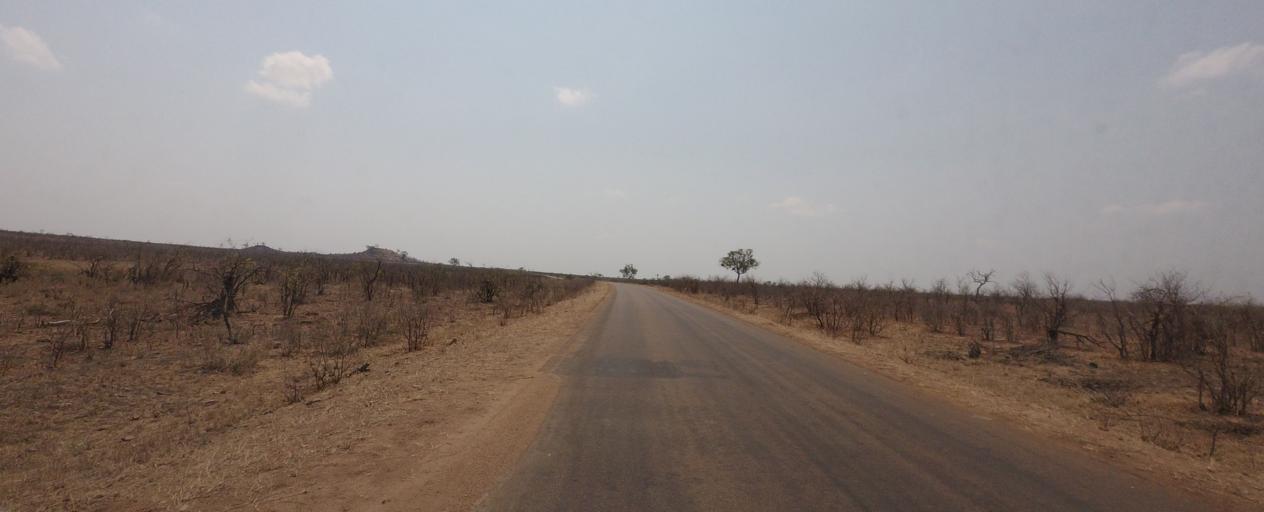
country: ZA
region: Limpopo
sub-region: Mopani District Municipality
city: Phalaborwa
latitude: -23.5027
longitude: 31.4037
